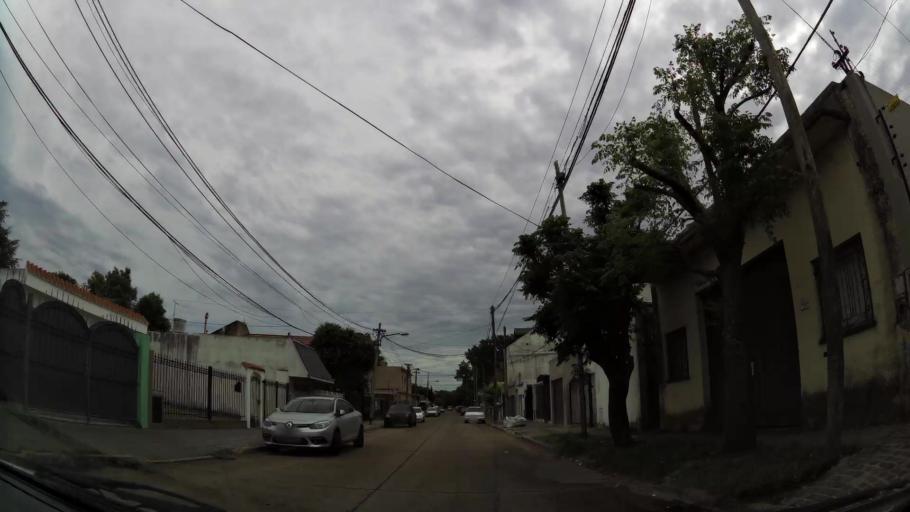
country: AR
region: Buenos Aires
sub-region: Partido de Quilmes
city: Quilmes
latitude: -34.7514
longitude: -58.2120
